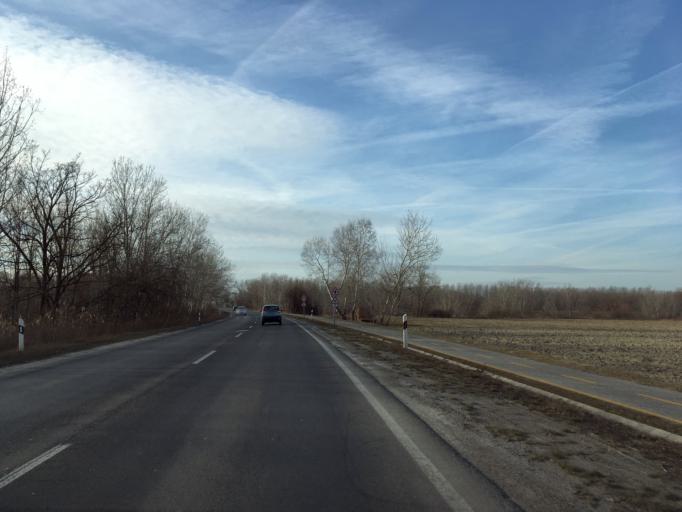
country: HU
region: Gyor-Moson-Sopron
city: Abda
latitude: 47.6856
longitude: 17.5666
